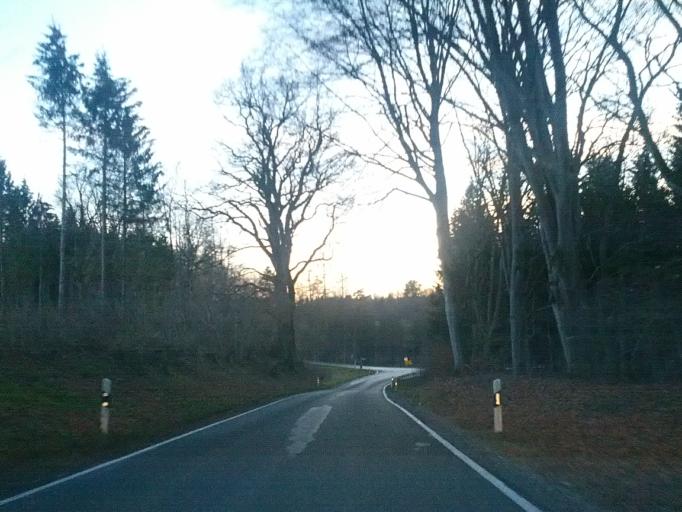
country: DE
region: Baden-Wuerttemberg
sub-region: Tuebingen Region
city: Aitrach
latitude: 47.9354
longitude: 10.0506
